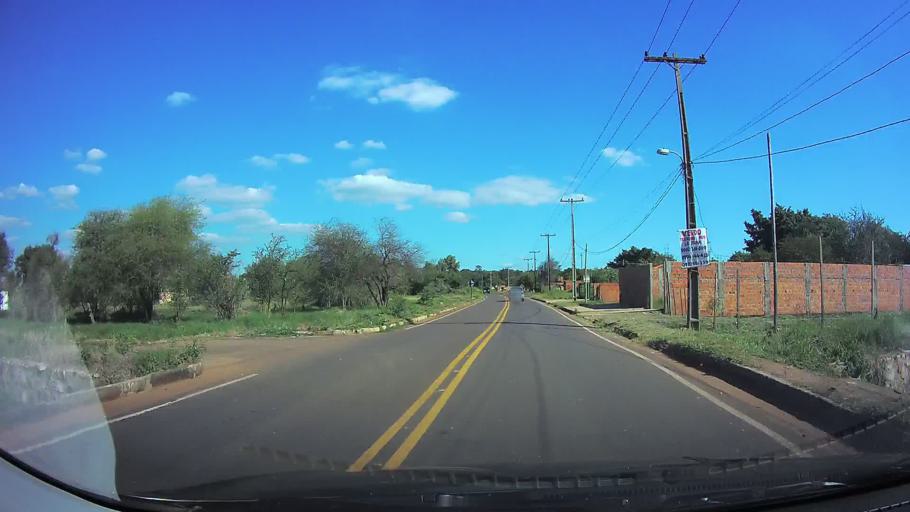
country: PY
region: Central
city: Limpio
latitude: -25.1915
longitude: -57.4757
